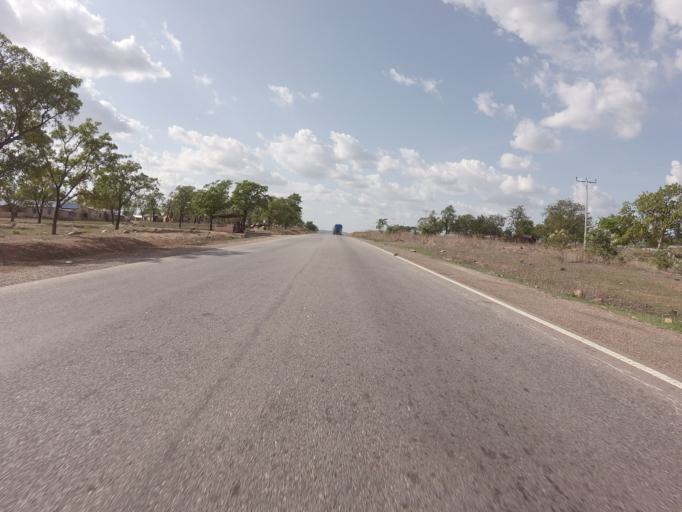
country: GH
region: Upper East
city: Bolgatanga
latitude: 10.5701
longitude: -0.8332
